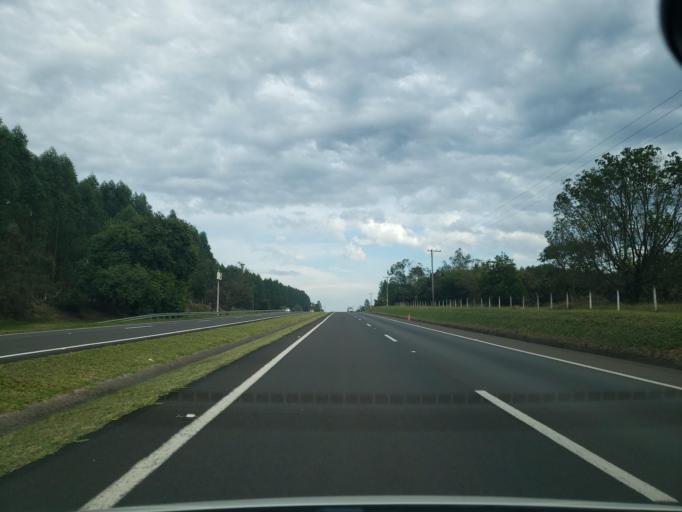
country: BR
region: Sao Paulo
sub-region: Itirapina
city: Itirapina
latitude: -22.2591
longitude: -47.8719
